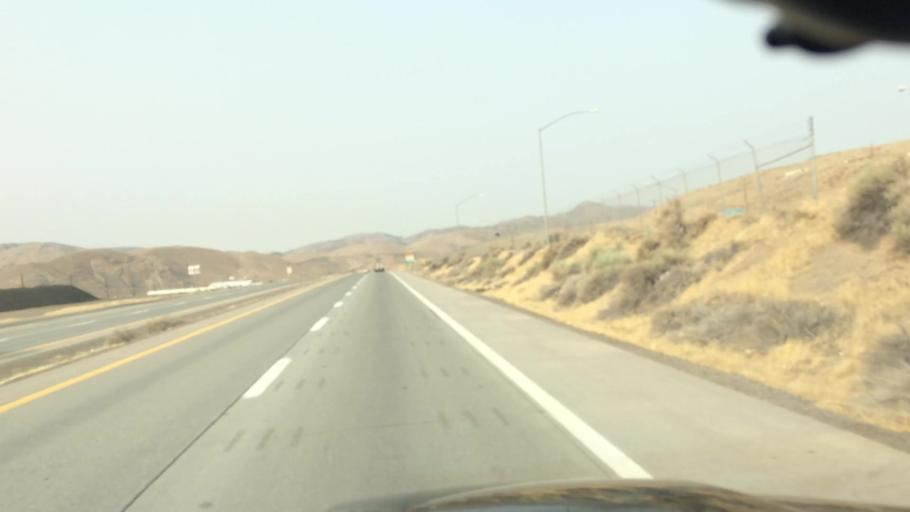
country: US
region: Nevada
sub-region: Washoe County
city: Sparks
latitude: 39.5258
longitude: -119.6207
